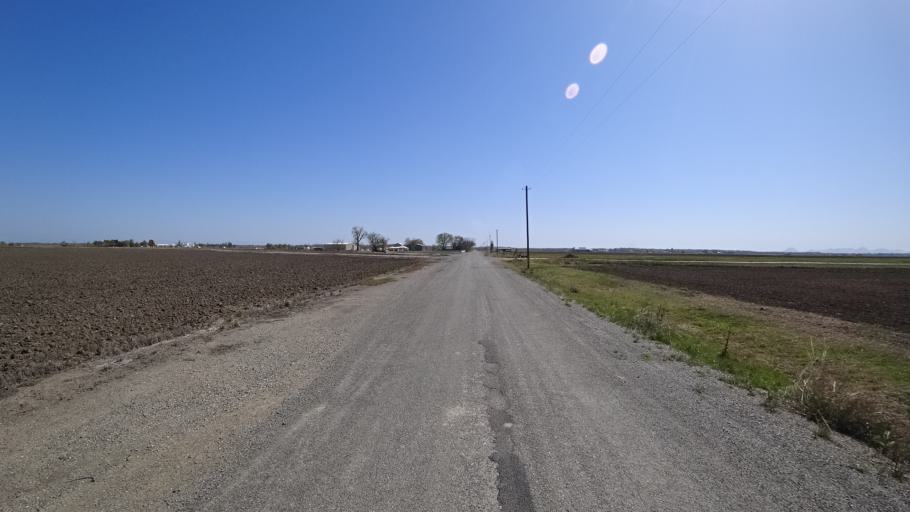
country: US
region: California
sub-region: Glenn County
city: Willows
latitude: 39.4431
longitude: -122.0437
